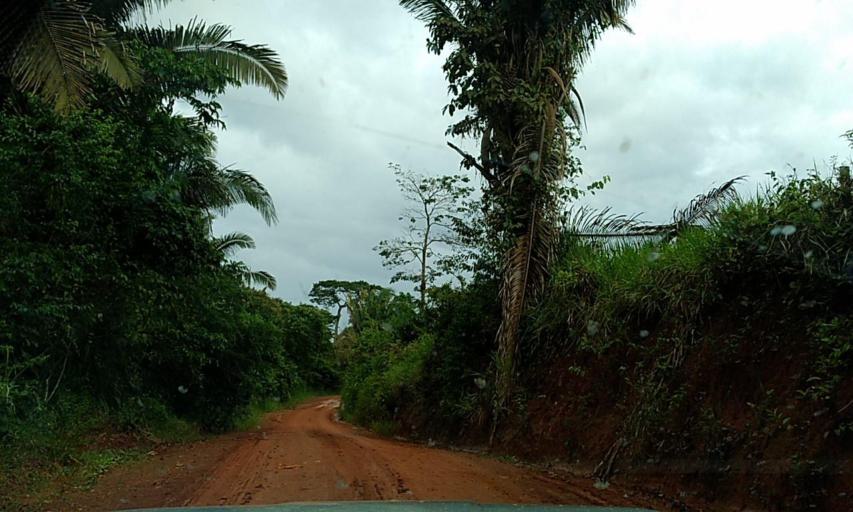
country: BR
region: Para
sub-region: Altamira
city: Altamira
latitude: -3.3076
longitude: -52.6884
